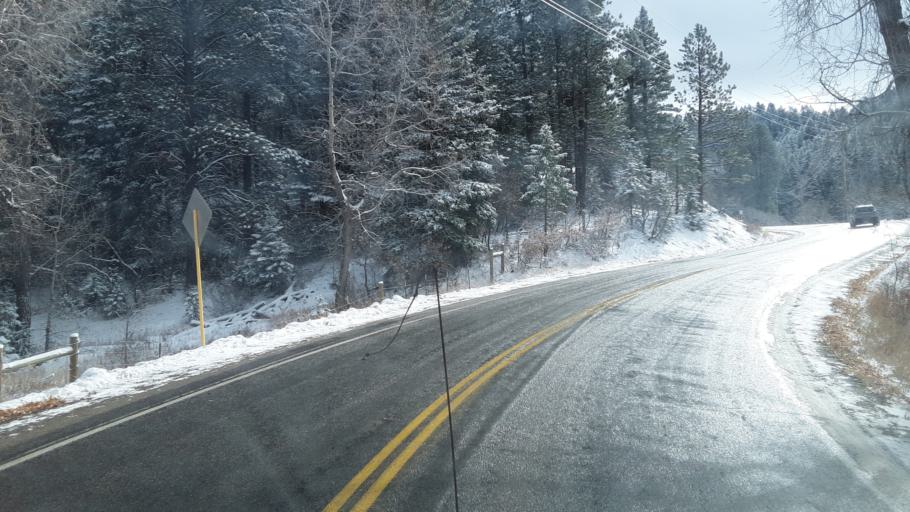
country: US
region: Colorado
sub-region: La Plata County
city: Bayfield
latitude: 37.3604
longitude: -107.6706
